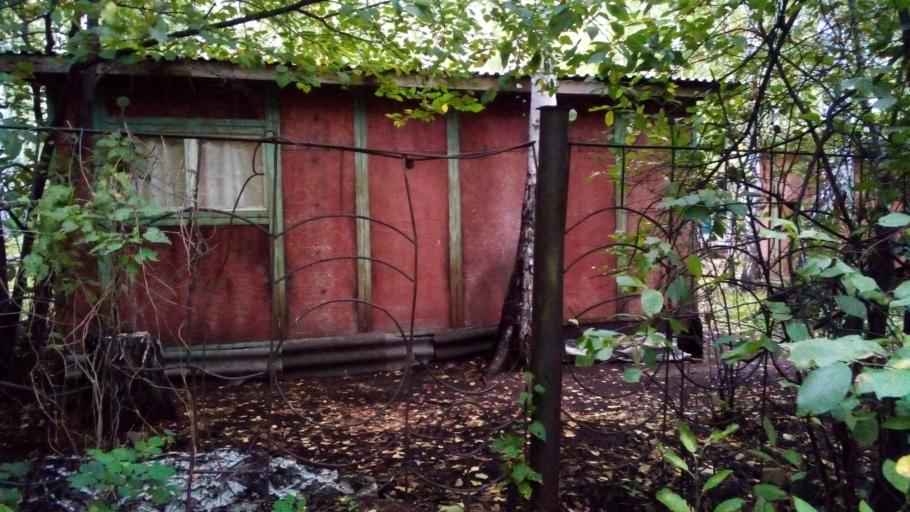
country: RU
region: Chelyabinsk
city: Tayginka
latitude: 55.4771
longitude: 60.5012
